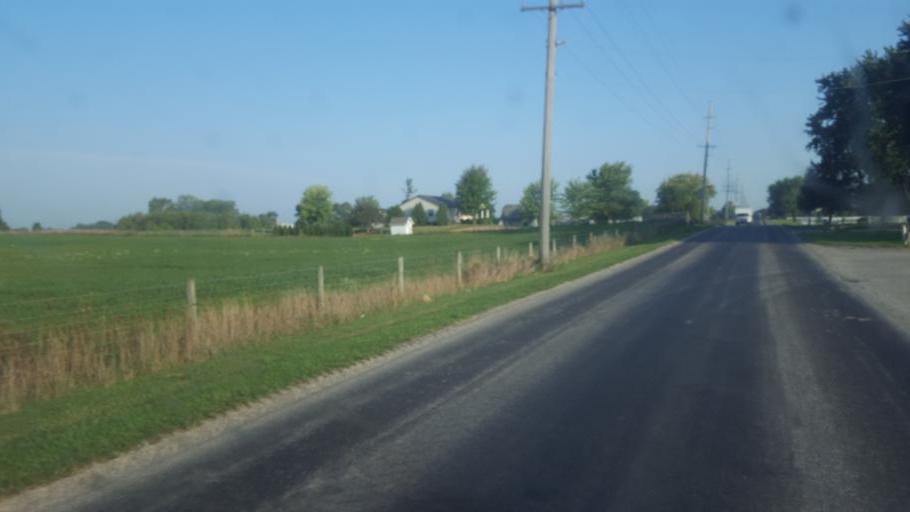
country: US
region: Indiana
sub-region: LaGrange County
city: Topeka
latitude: 41.6596
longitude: -85.5561
